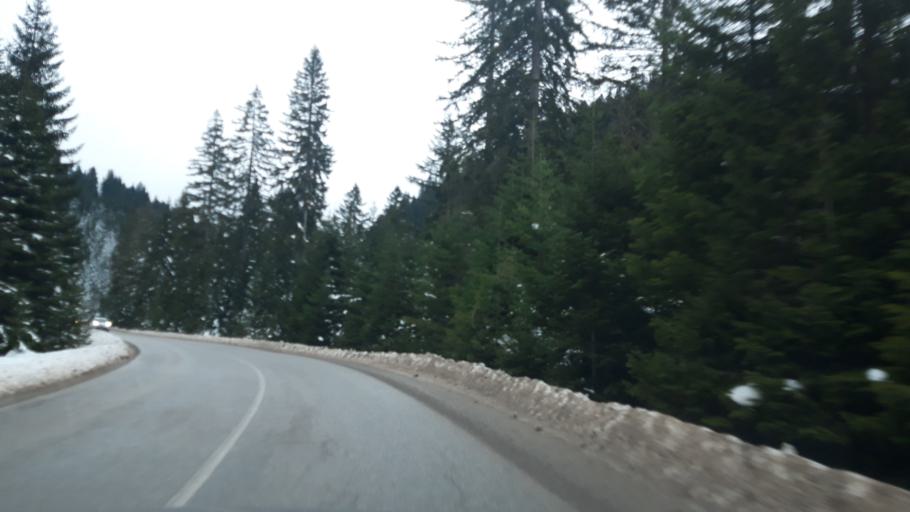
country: BA
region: Republika Srpska
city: Koran
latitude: 43.7712
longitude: 18.5487
